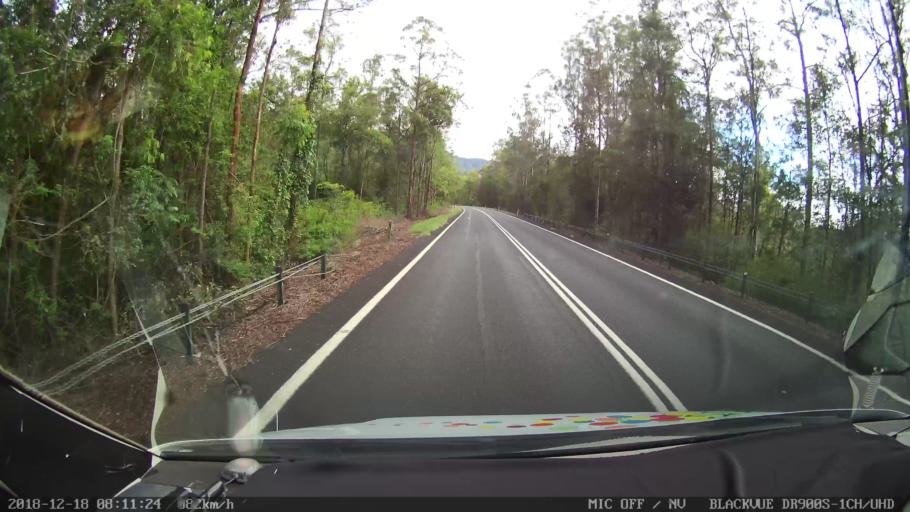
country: AU
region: New South Wales
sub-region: Kyogle
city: Kyogle
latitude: -28.3513
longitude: 152.6687
